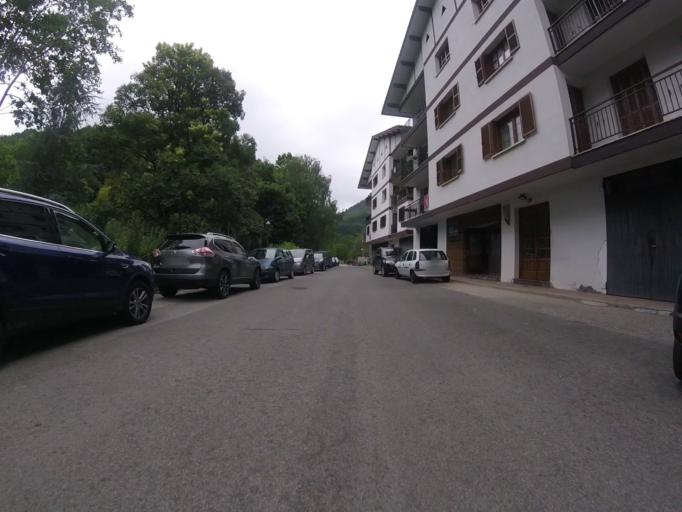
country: ES
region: Navarre
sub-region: Provincia de Navarra
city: Doneztebe
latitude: 43.1343
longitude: -1.6659
